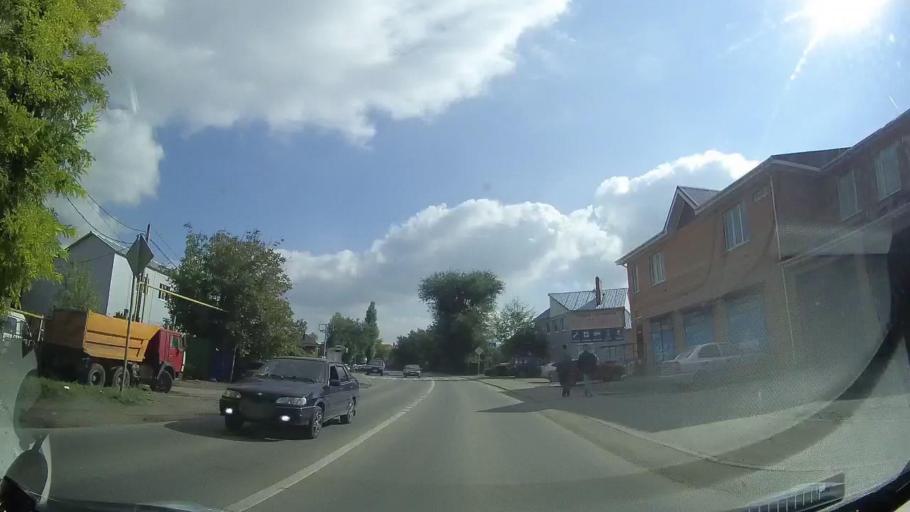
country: RU
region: Rostov
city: Severnyy
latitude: 47.2857
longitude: 39.6672
